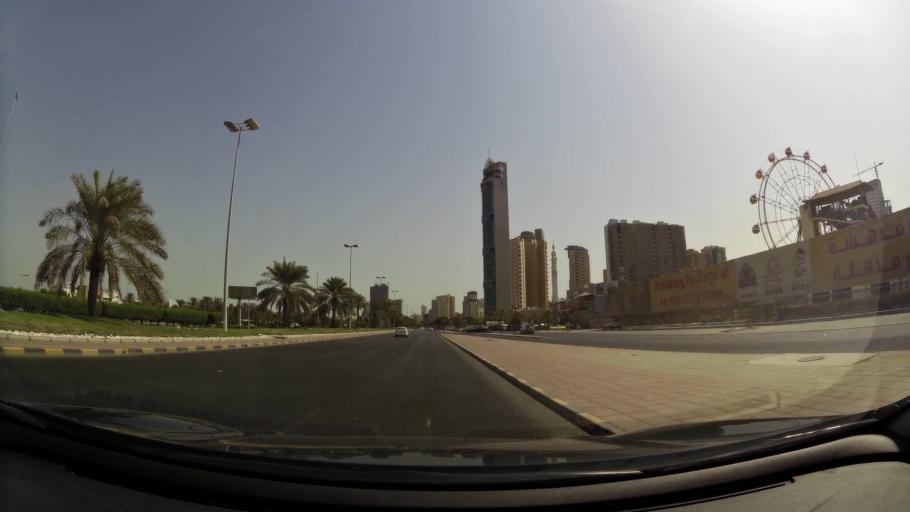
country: KW
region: Muhafazat Hawalli
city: Hawalli
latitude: 29.3438
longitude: 48.0448
